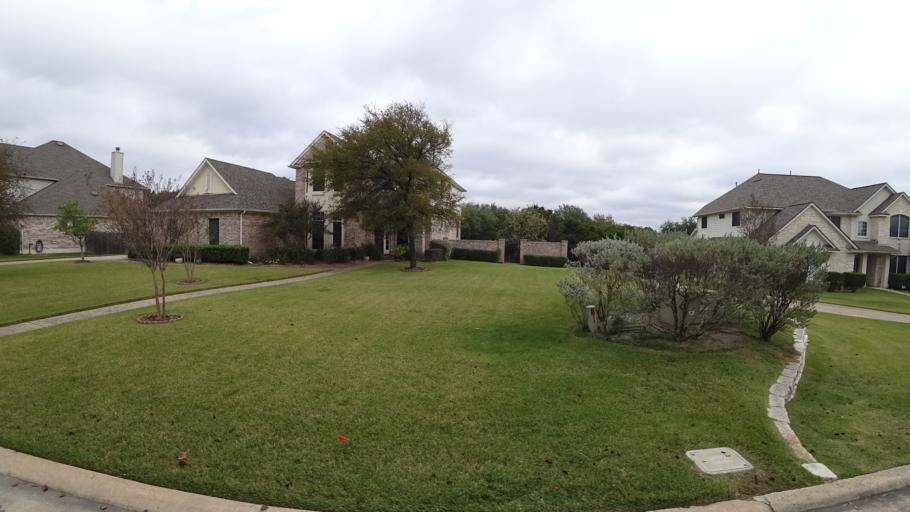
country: US
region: Texas
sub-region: Travis County
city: Barton Creek
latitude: 30.2563
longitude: -97.9071
